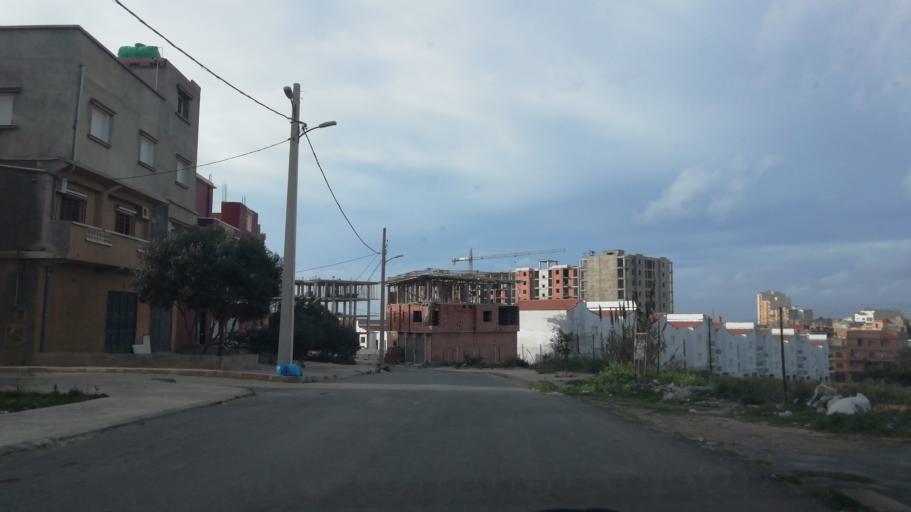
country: DZ
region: Oran
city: Bir el Djir
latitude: 35.7312
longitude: -0.5691
